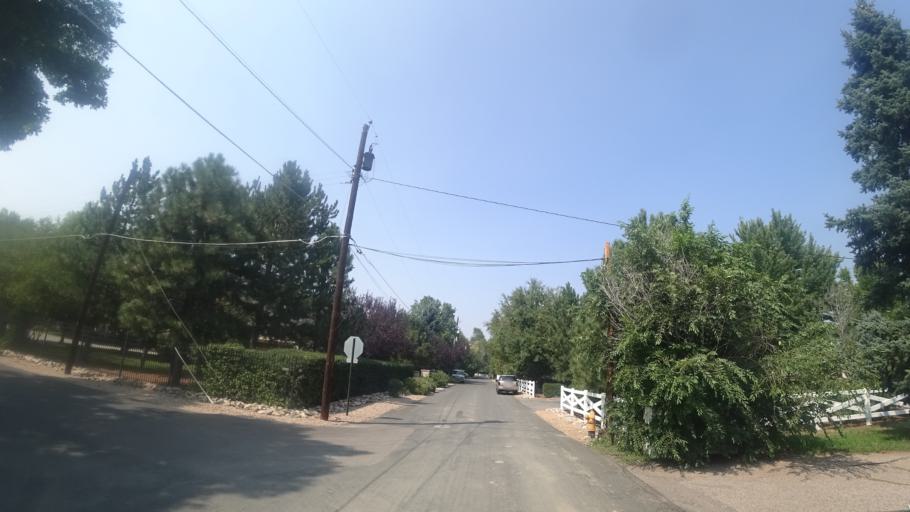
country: US
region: Colorado
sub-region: Arapahoe County
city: Cherry Hills Village
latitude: 39.6368
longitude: -104.9738
